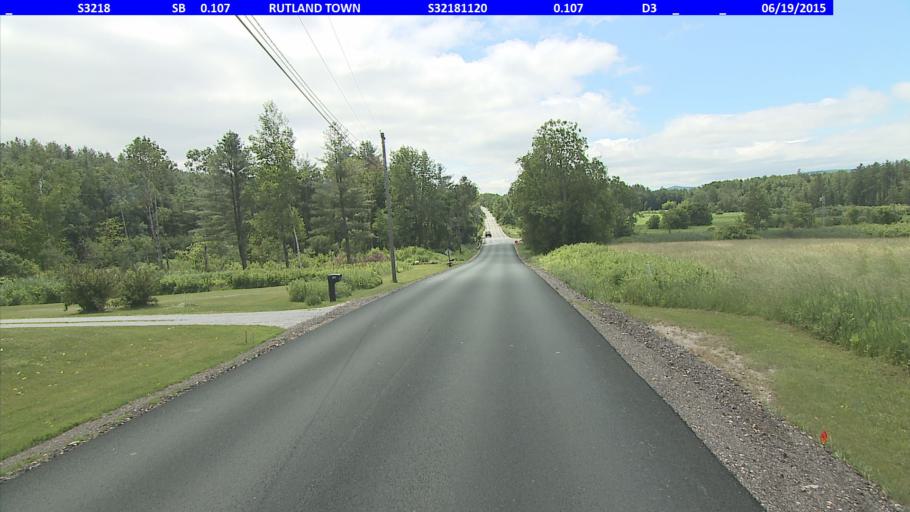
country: US
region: Vermont
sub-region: Rutland County
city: Rutland
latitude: 43.5876
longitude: -72.9514
